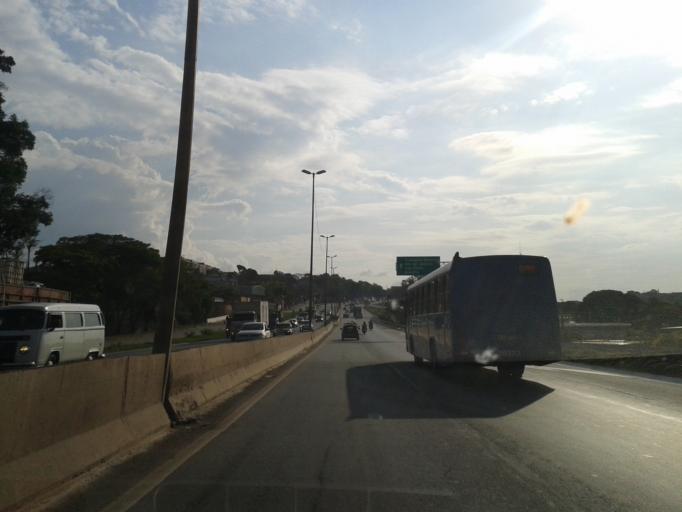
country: BR
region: Minas Gerais
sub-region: Belo Horizonte
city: Belo Horizonte
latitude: -19.8689
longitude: -43.9398
